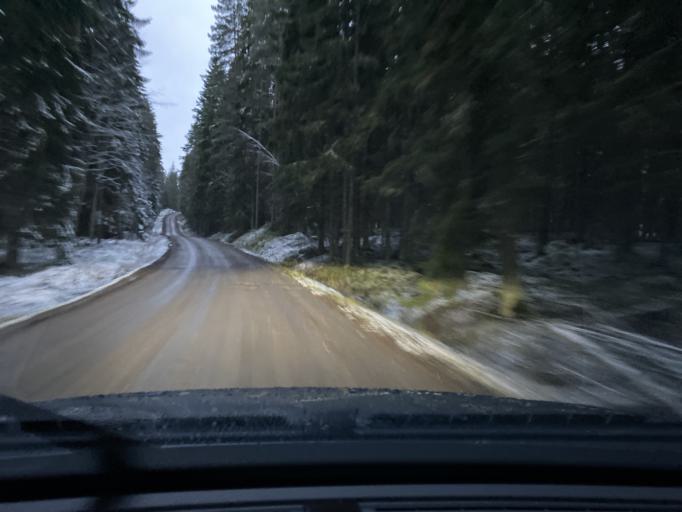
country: FI
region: Pirkanmaa
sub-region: Lounais-Pirkanmaa
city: Punkalaidun
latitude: 61.1556
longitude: 22.9463
